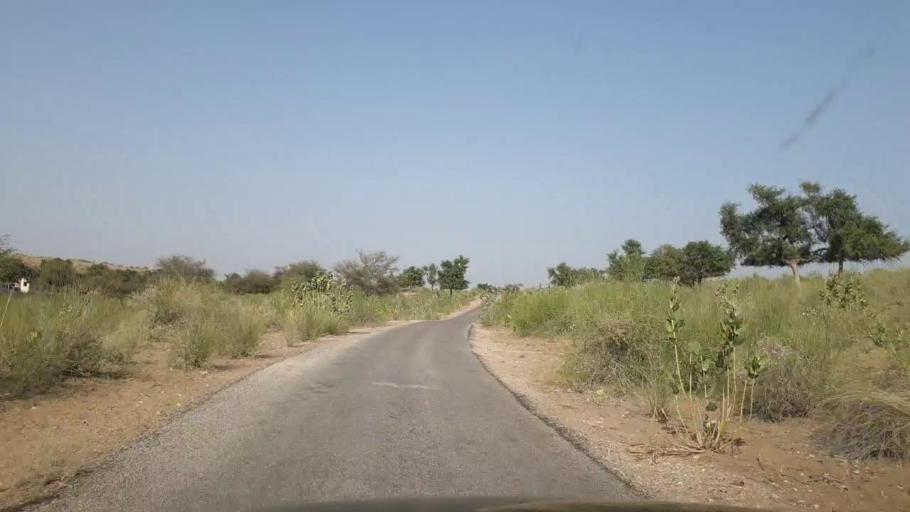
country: PK
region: Sindh
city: Islamkot
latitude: 25.1108
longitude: 70.4262
